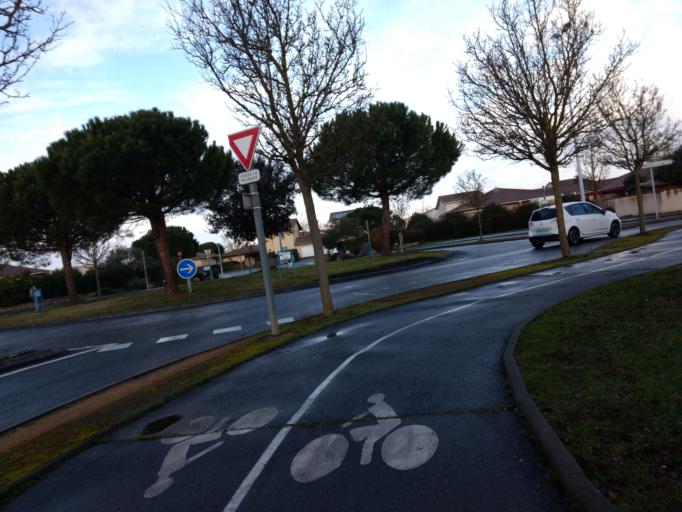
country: FR
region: Midi-Pyrenees
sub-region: Departement de la Haute-Garonne
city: Tournefeuille
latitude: 43.5957
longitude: 1.3205
